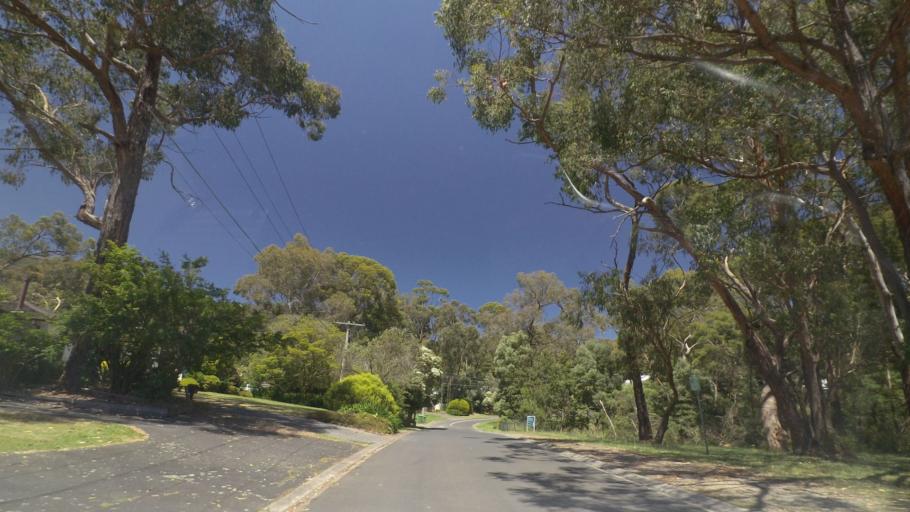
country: AU
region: Victoria
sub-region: Yarra Ranges
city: Montrose
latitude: -37.8093
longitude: 145.3554
